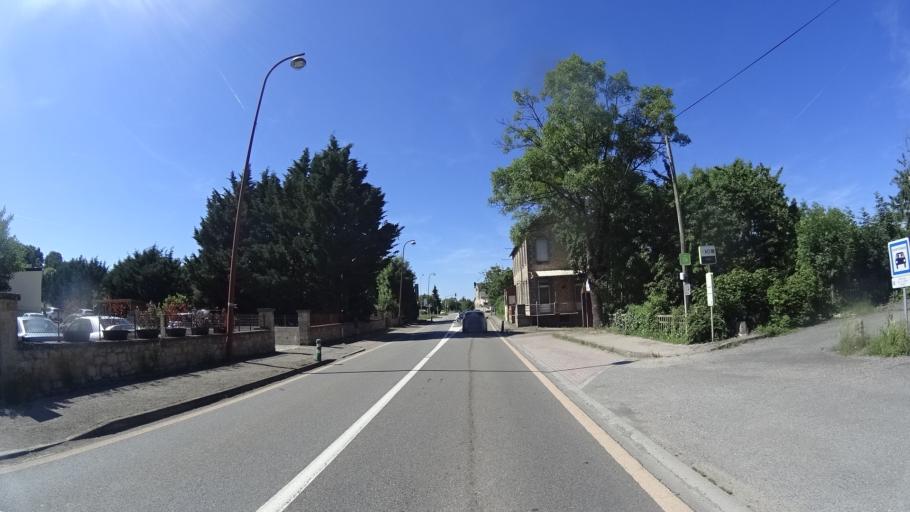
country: FR
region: Midi-Pyrenees
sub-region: Departement de l'Aveyron
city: Valady
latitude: 44.4402
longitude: 2.4411
